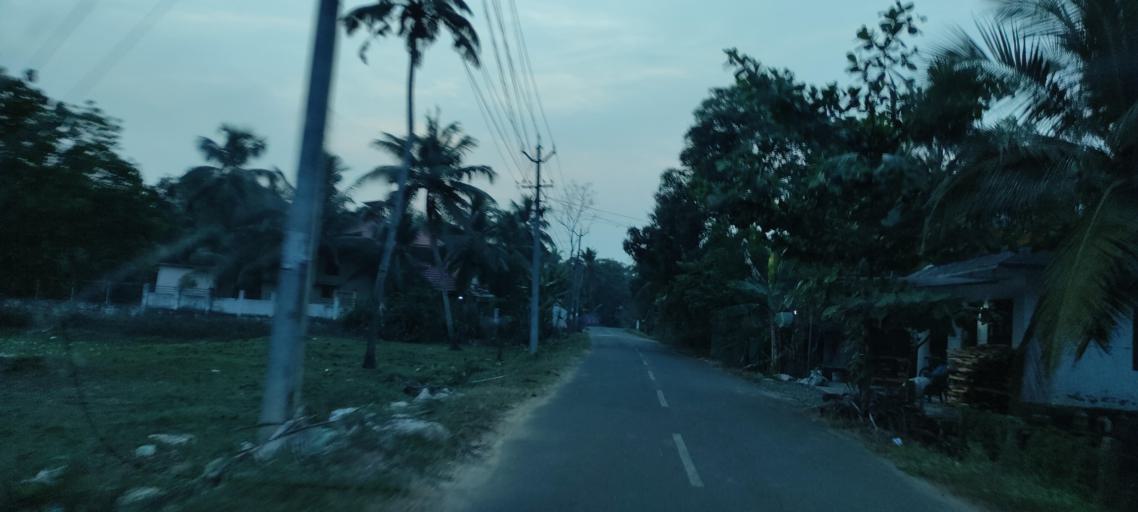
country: IN
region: Kerala
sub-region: Pattanamtitta
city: Tiruvalla
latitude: 9.3317
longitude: 76.5075
